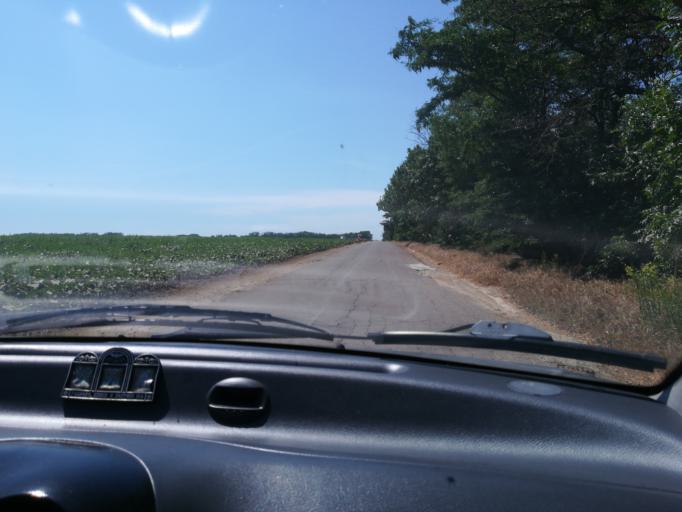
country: RU
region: Krasnodarskiy
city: Blagovetschenskaya
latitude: 45.0569
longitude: 37.1083
